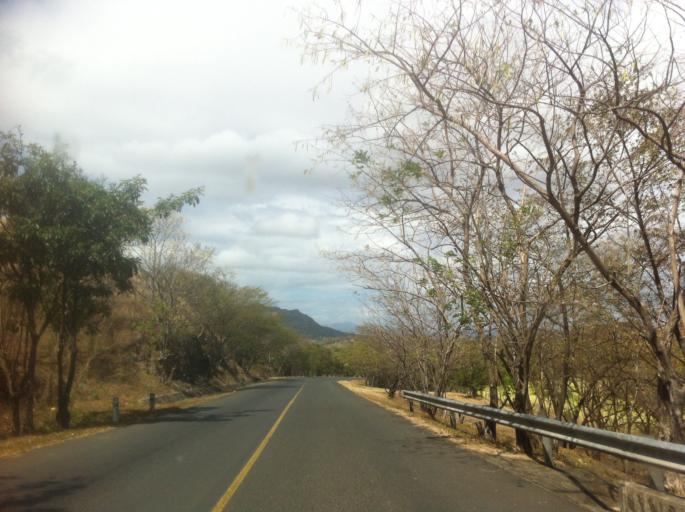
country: NI
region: Chontales
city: Juigalpa
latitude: 12.0428
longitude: -85.2783
